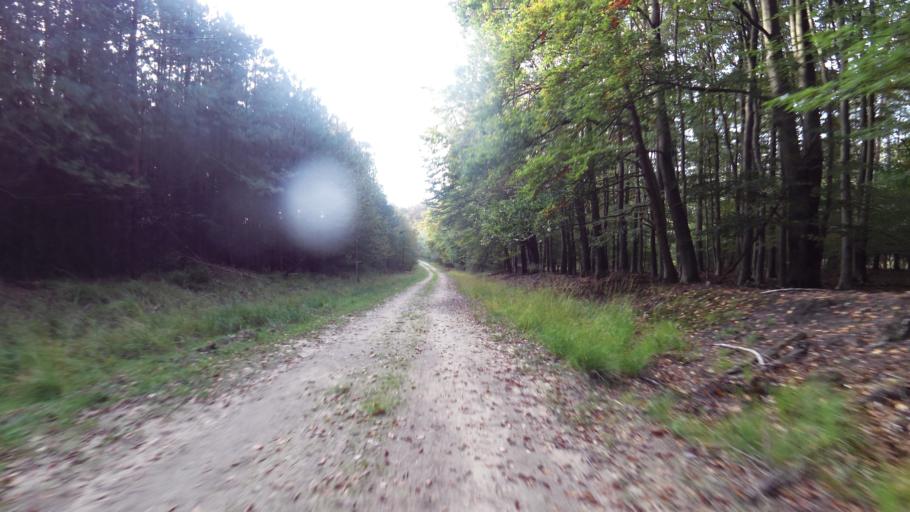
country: NL
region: Gelderland
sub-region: Gemeente Apeldoorn
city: Uddel
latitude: 52.3089
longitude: 5.8470
